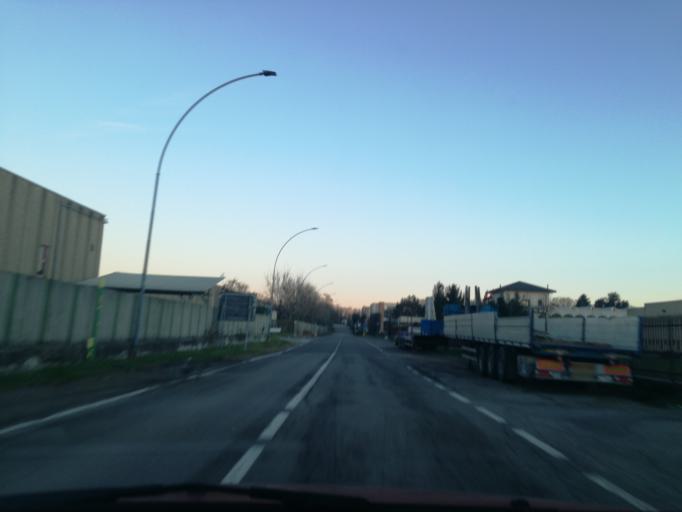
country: IT
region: Lombardy
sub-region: Provincia di Lecco
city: Osnago
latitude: 45.6717
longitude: 9.3925
